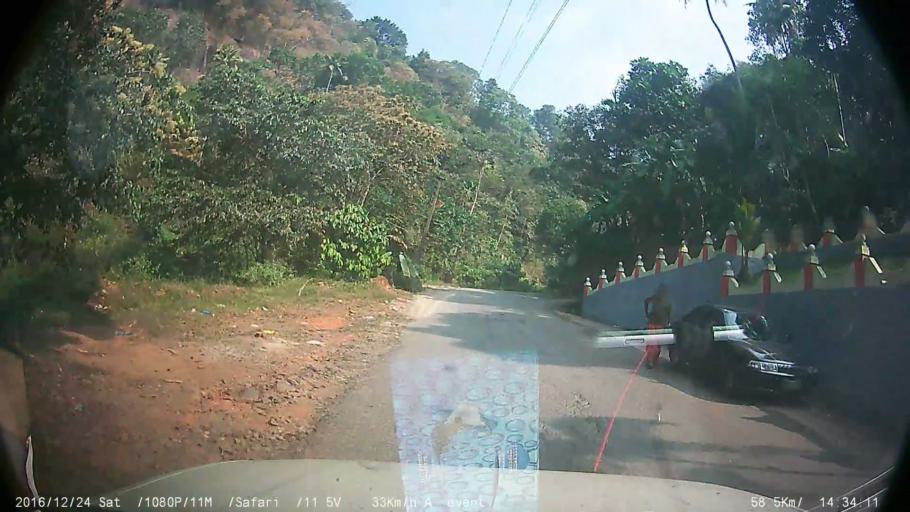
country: IN
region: Kerala
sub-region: Kottayam
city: Lalam
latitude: 9.8138
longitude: 76.7264
